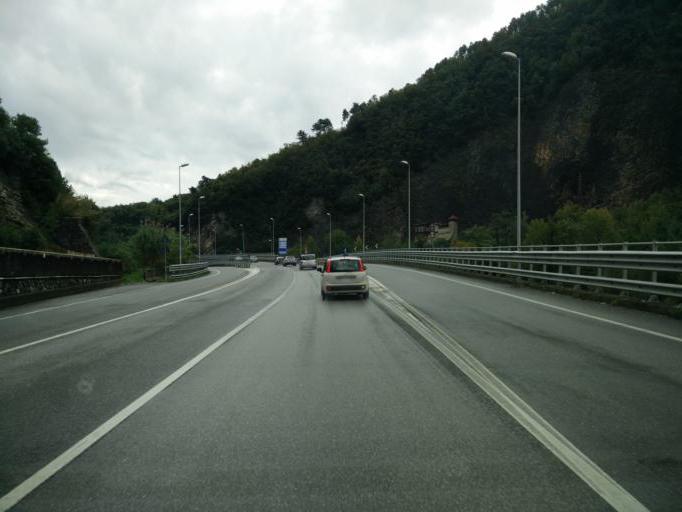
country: IT
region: Tuscany
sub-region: Provincia di Lucca
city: Valdottavo
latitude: 43.9272
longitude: 10.5171
